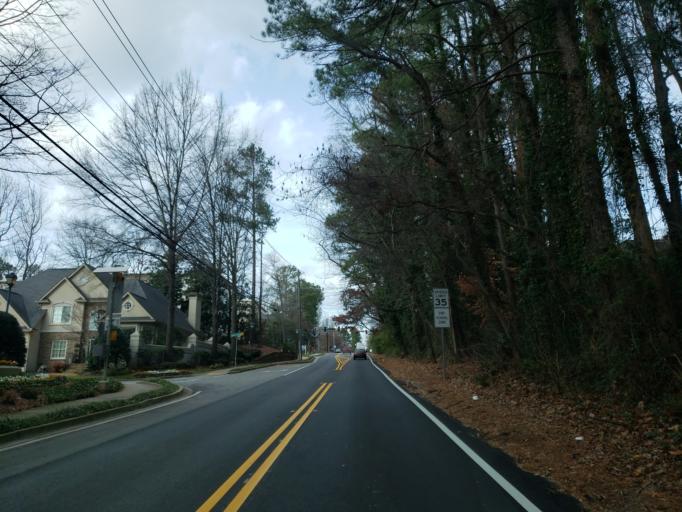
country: US
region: Georgia
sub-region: Fulton County
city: Sandy Springs
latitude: 33.9179
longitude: -84.3871
